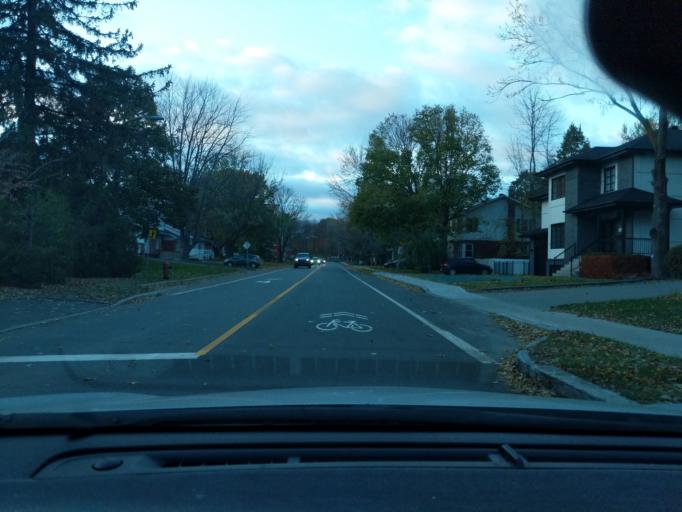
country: CA
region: Quebec
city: Quebec
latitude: 46.7732
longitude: -71.2713
